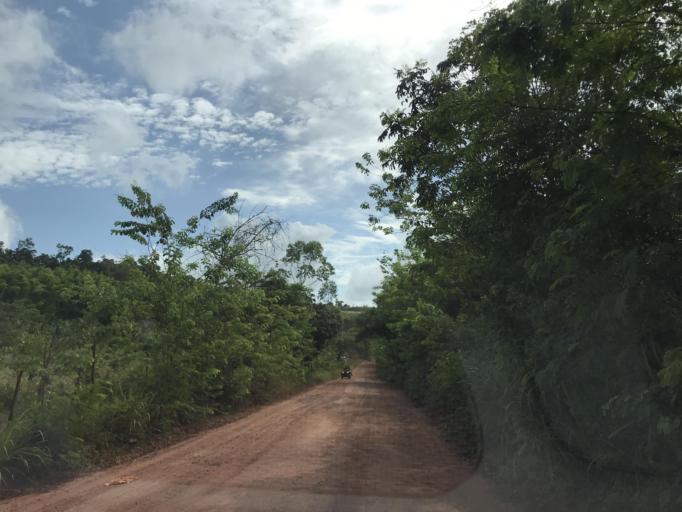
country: BR
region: Bahia
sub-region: Entre Rios
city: Entre Rios
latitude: -12.1647
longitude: -38.1643
